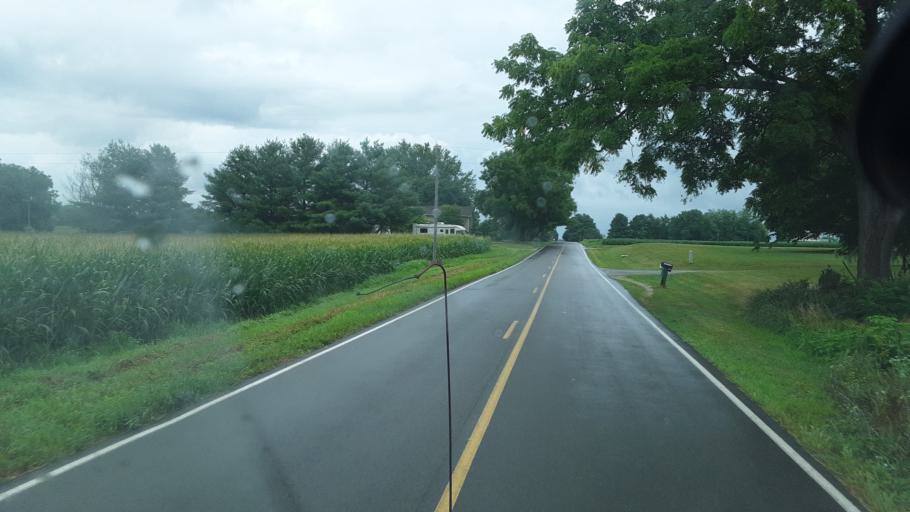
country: US
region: Indiana
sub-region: Steuben County
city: Hamilton
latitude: 41.6158
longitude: -84.8332
